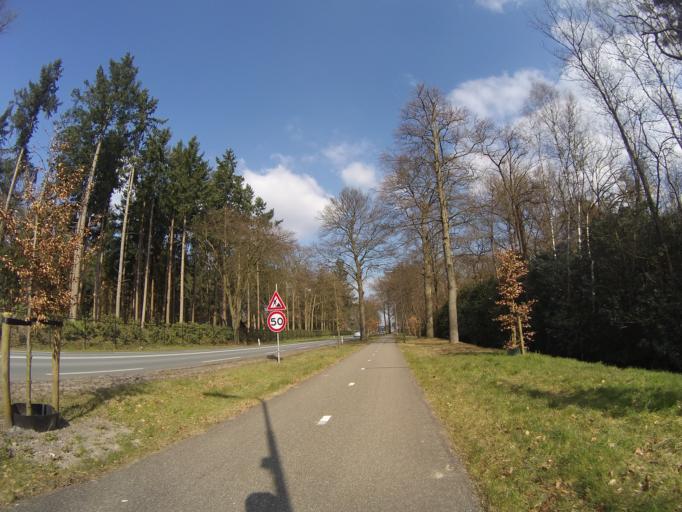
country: NL
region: Utrecht
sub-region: Gemeente Soest
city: Soest
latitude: 52.1635
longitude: 5.2364
